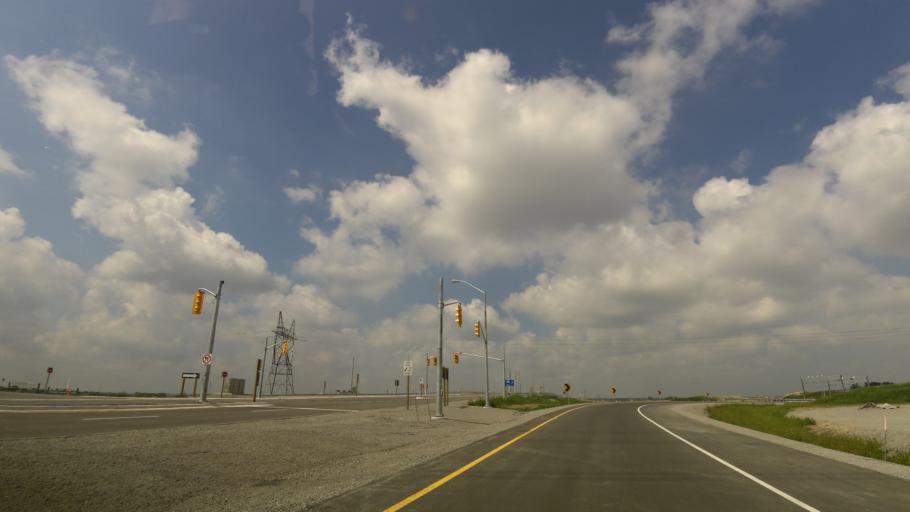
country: CA
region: Ontario
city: Oshawa
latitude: 43.9492
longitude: -78.9397
